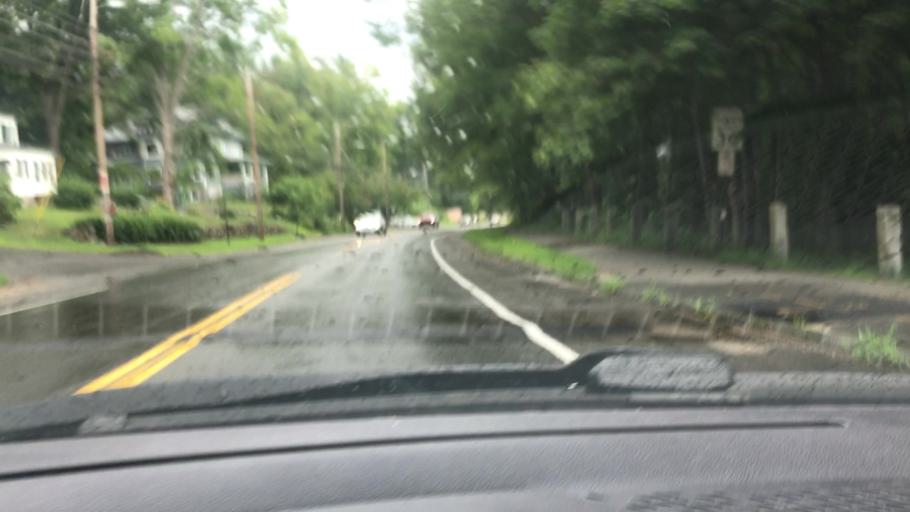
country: US
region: New Hampshire
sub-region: Merrimack County
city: Concord
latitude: 43.1972
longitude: -71.5566
